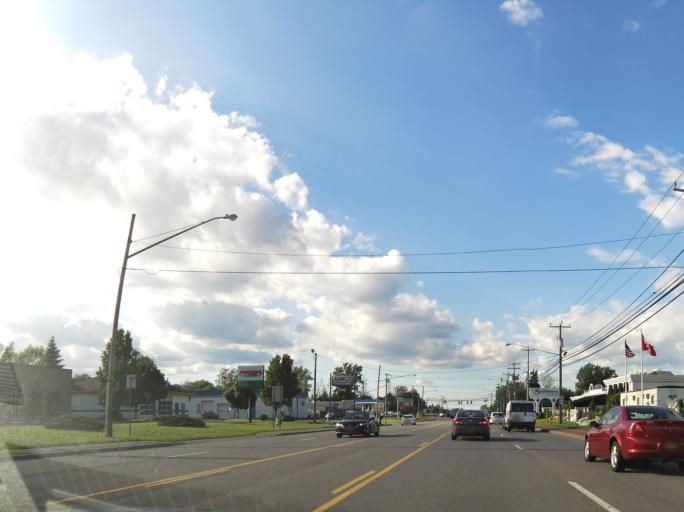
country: US
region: New York
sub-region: Erie County
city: Depew
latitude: 42.9360
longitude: -78.6969
